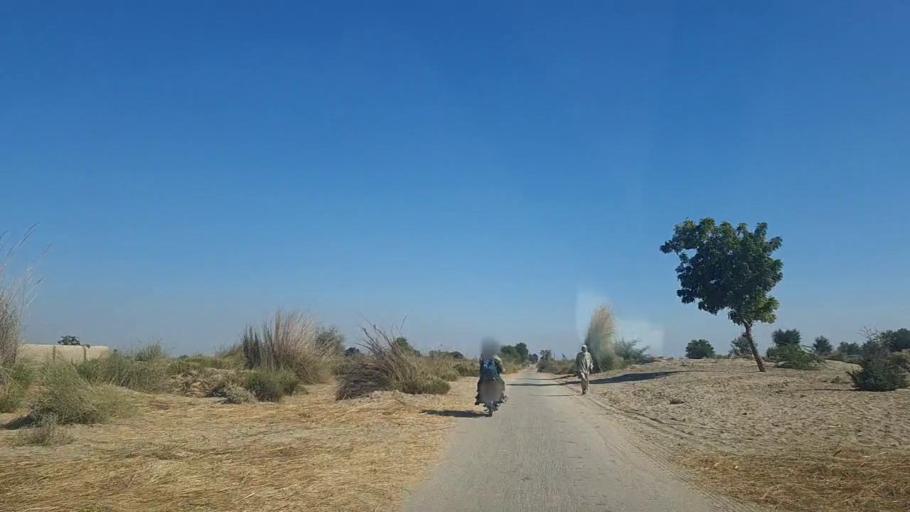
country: PK
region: Sindh
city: Khadro
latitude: 26.2094
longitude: 68.8419
